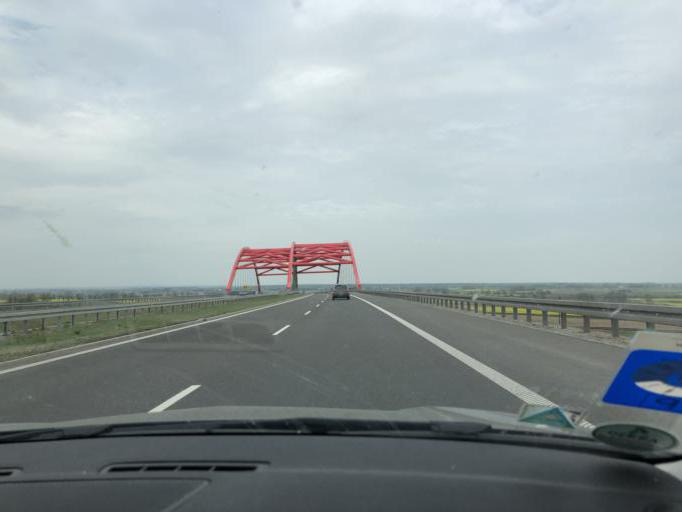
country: PL
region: Subcarpathian Voivodeship
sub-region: Powiat przeworski
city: Rozborz
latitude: 50.0616
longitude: 22.5663
